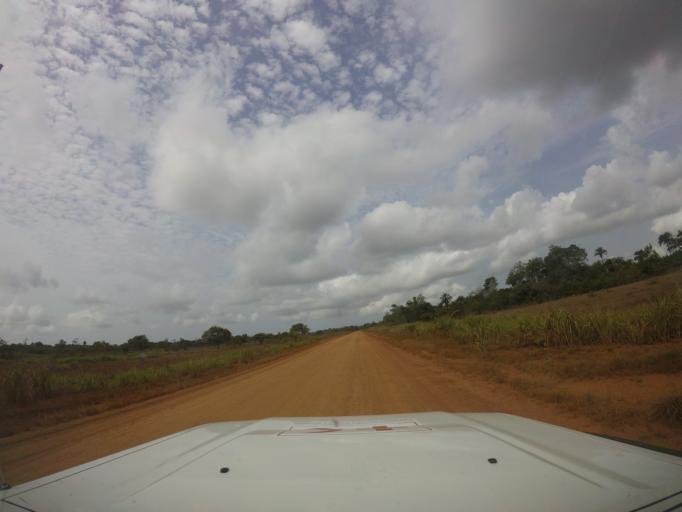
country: LR
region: Grand Cape Mount
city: Robertsport
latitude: 6.6924
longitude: -11.1094
